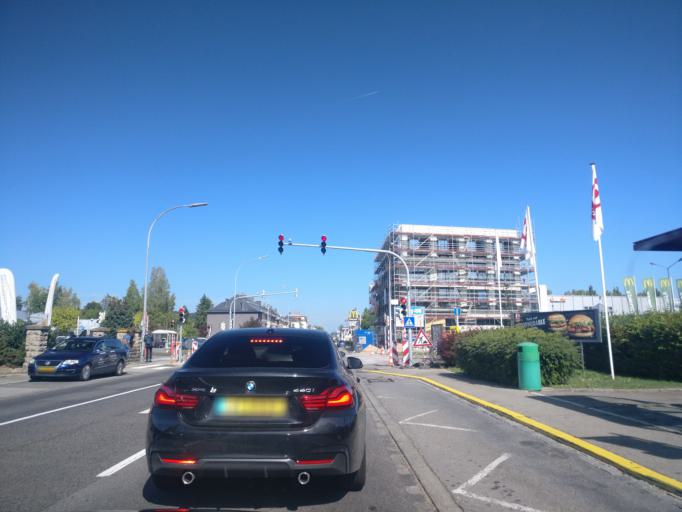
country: LU
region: Luxembourg
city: Bereldange
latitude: 49.6495
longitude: 6.1278
